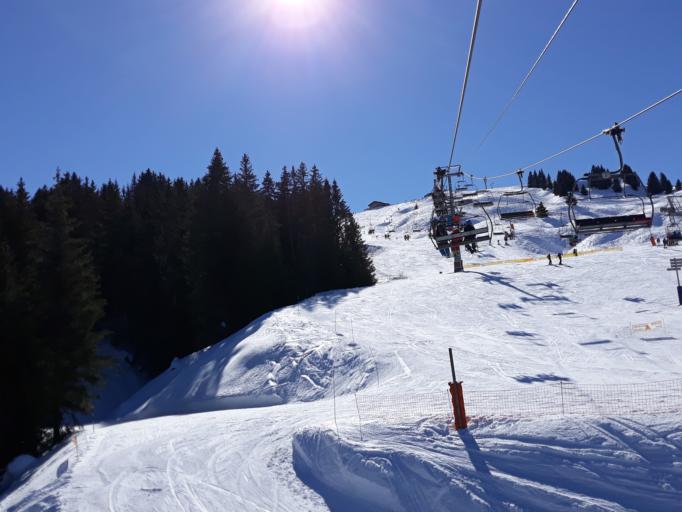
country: FR
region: Rhone-Alpes
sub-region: Departement de la Haute-Savoie
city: Araches-la-Frasse
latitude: 46.0483
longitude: 6.6693
